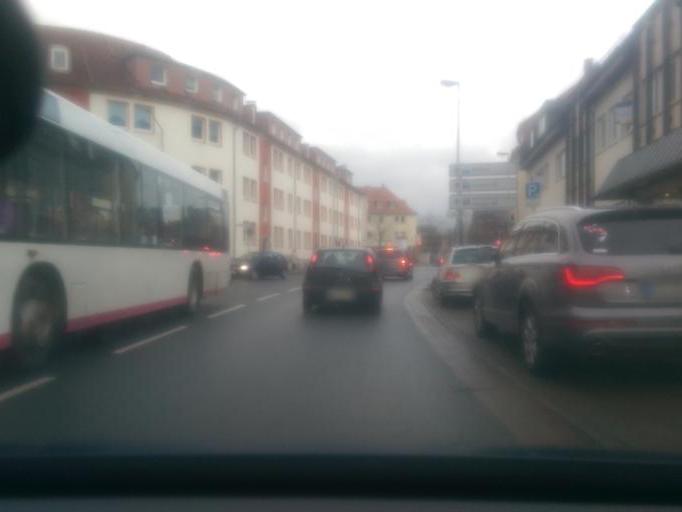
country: DE
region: Lower Saxony
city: Hameln
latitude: 52.1106
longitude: 9.3544
